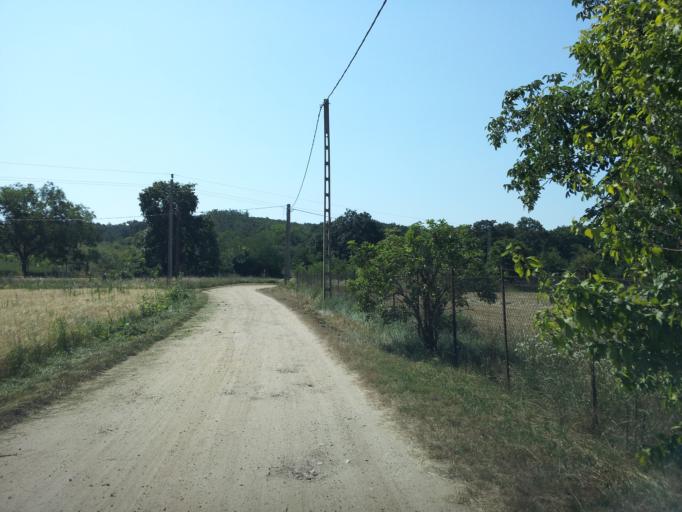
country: HU
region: Fejer
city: Pakozd
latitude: 47.2553
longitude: 18.5144
